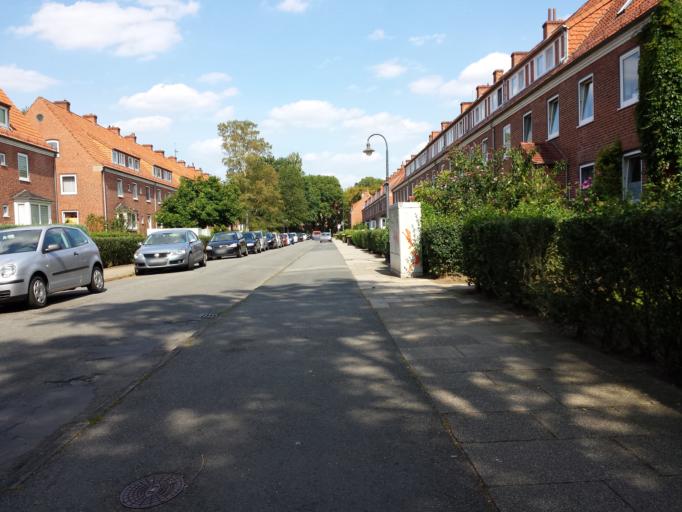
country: DE
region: Bremen
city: Bremen
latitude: 53.0409
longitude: 8.8177
